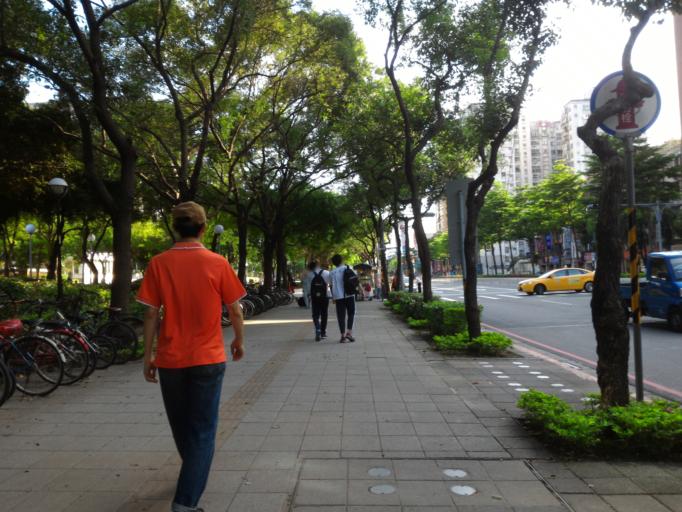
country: TW
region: Taipei
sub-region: Taipei
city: Banqiao
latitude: 25.0155
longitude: 121.4627
